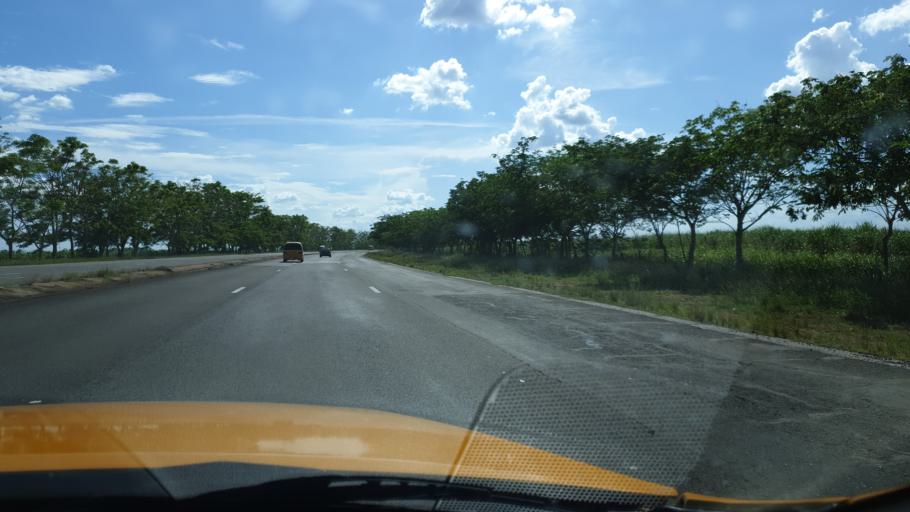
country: CU
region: Cienfuegos
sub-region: Municipio de Aguada de Pasajeros
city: Aguada de Pasajeros
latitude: 22.4024
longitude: -80.8494
